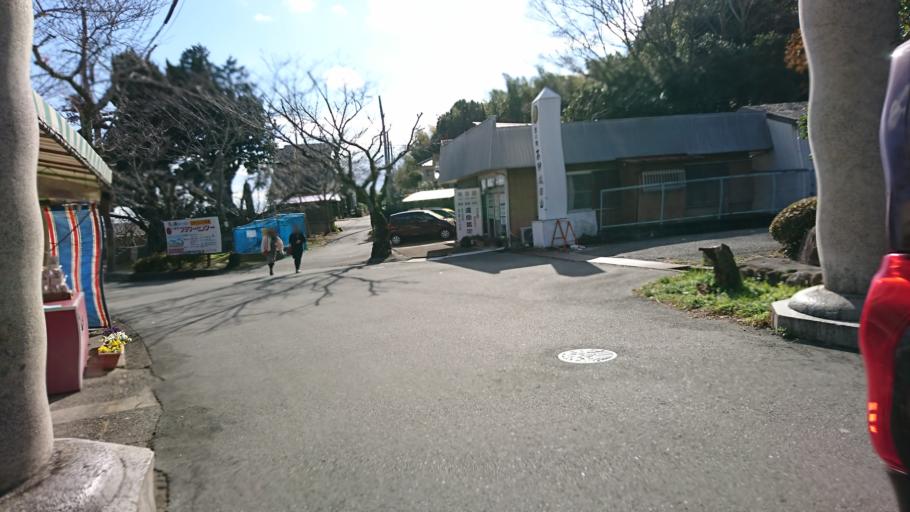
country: JP
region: Hyogo
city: Shirahamacho-usazakiminami
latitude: 34.8086
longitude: 134.7757
